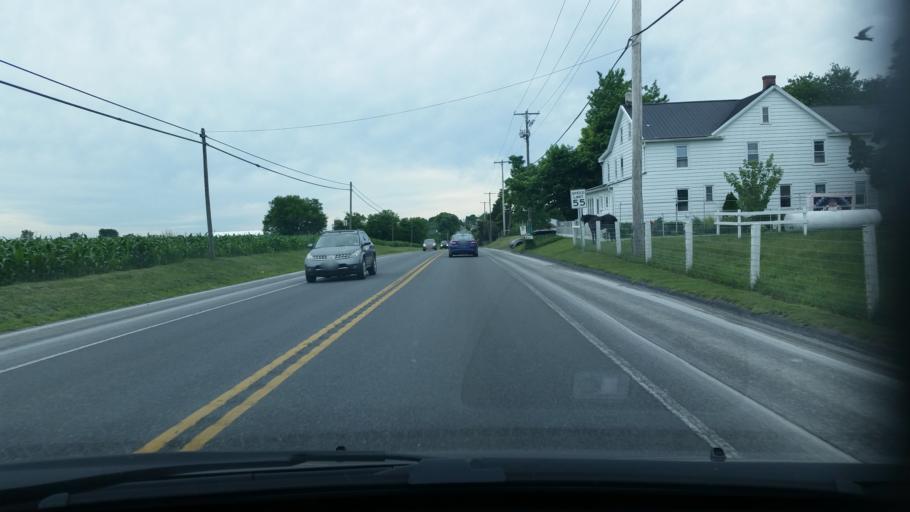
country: US
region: Pennsylvania
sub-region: Lancaster County
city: Paradise
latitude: 40.0388
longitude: -76.1462
